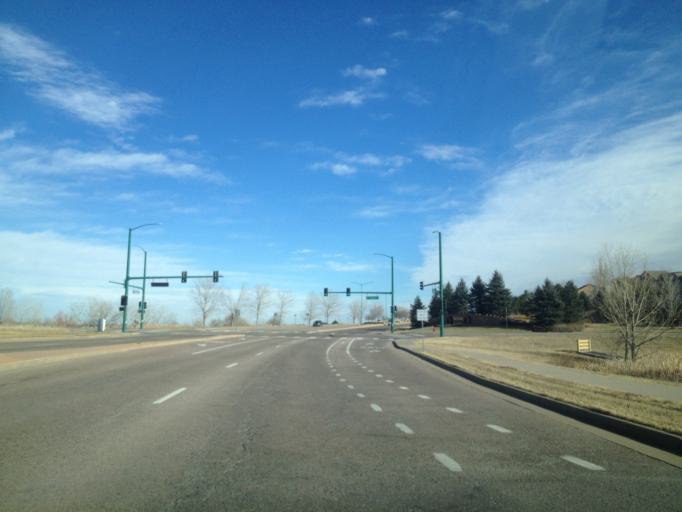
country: US
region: Colorado
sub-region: Boulder County
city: Superior
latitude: 39.9290
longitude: -105.1609
